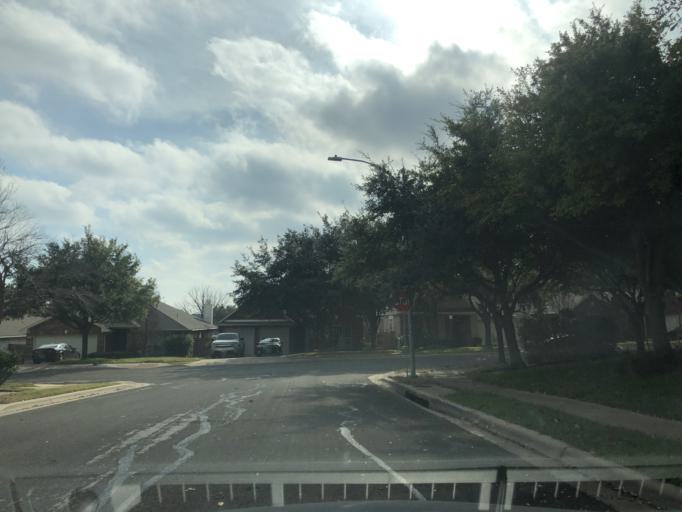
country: US
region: Texas
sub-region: Travis County
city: Wells Branch
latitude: 30.4252
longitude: -97.6802
